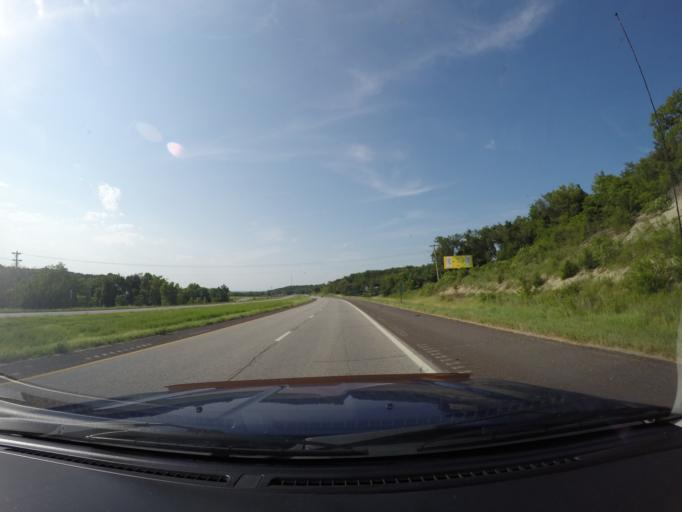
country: US
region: Kansas
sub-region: Riley County
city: Manhattan
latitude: 39.1590
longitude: -96.5385
